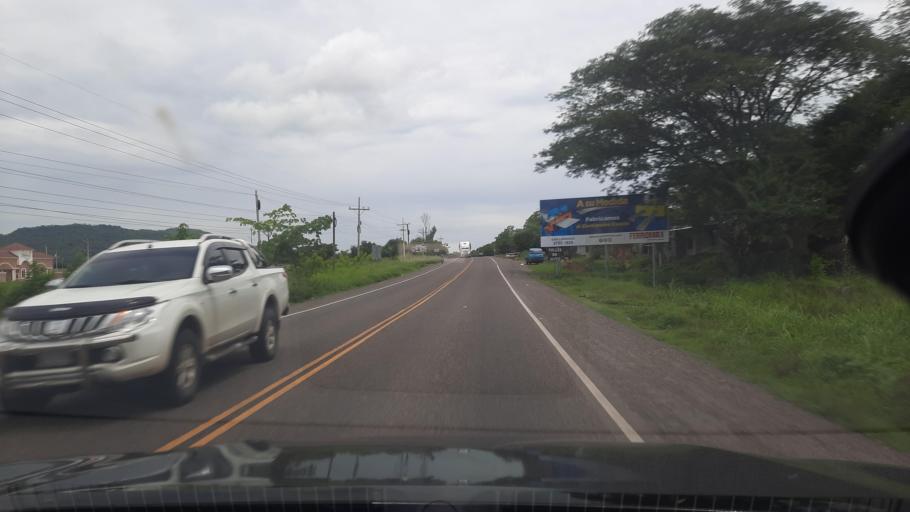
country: HN
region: Valle
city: Jicaro Galan
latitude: 13.5078
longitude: -87.4410
